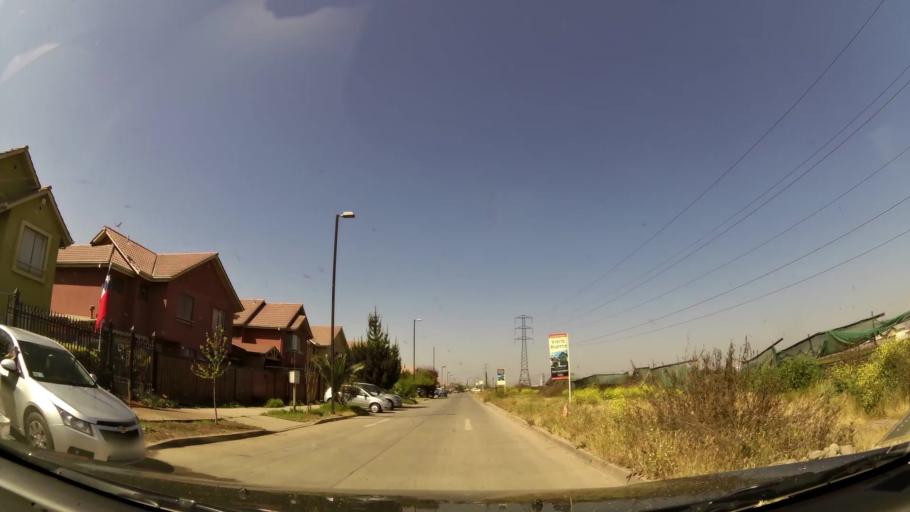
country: CL
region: Santiago Metropolitan
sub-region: Provincia de Chacabuco
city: Chicureo Abajo
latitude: -33.3249
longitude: -70.7551
